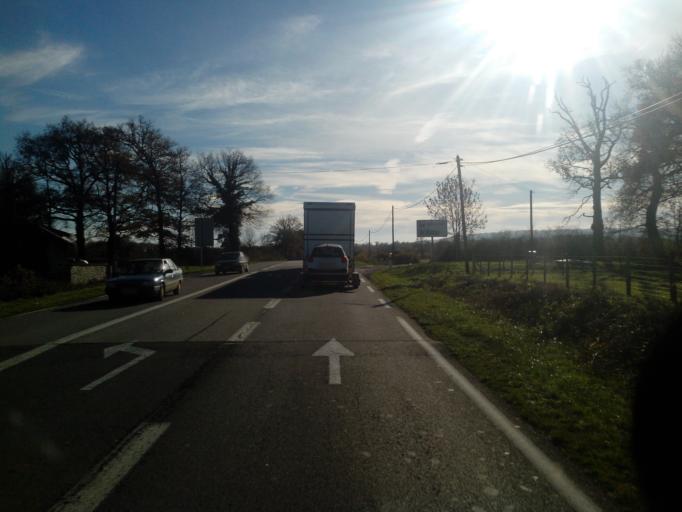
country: FR
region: Limousin
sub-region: Departement de la Haute-Vienne
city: Bellac
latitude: 46.1062
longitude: 1.0740
